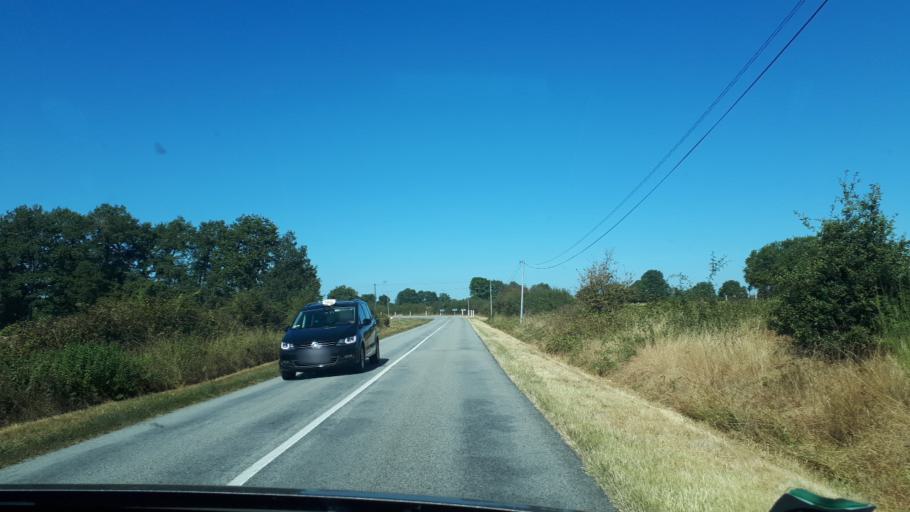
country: FR
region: Centre
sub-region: Departement du Loiret
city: Coullons
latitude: 47.6374
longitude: 2.4460
